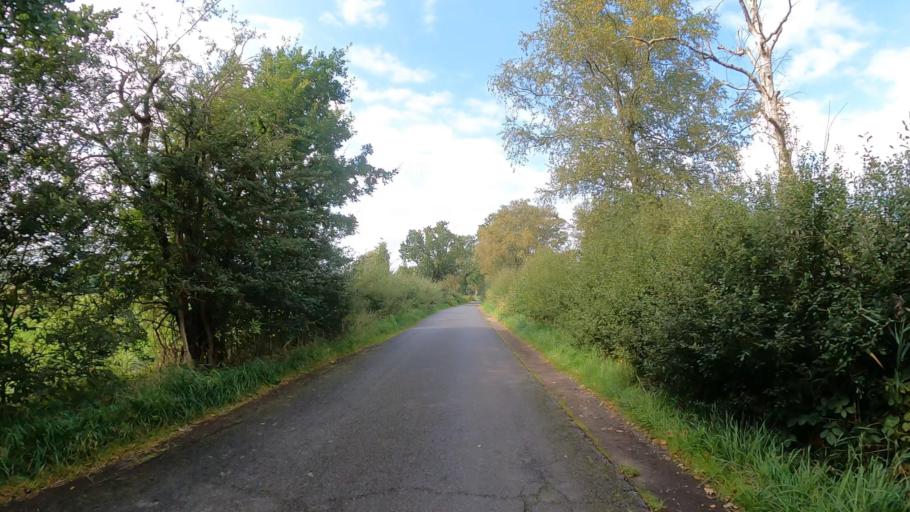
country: DE
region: Schleswig-Holstein
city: Tornesch
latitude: 53.7222
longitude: 9.6984
